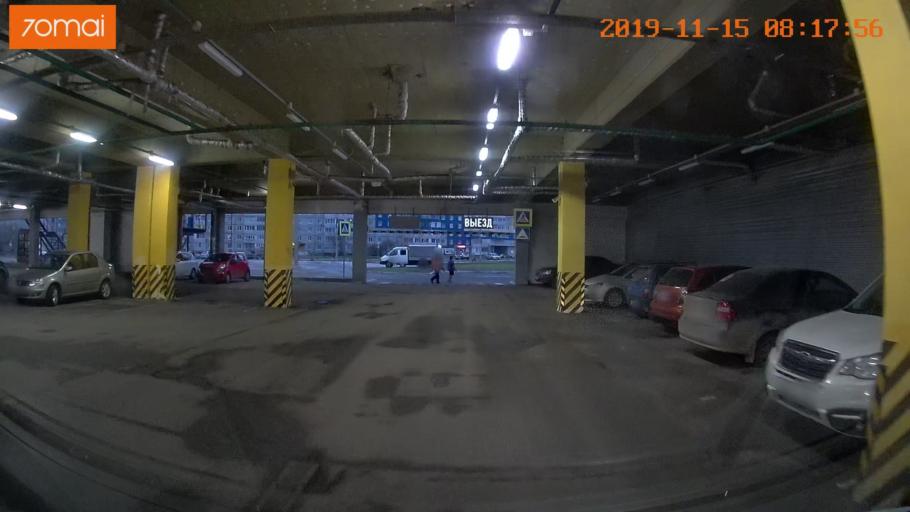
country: RU
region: Vologda
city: Cherepovets
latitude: 59.0923
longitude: 37.9181
